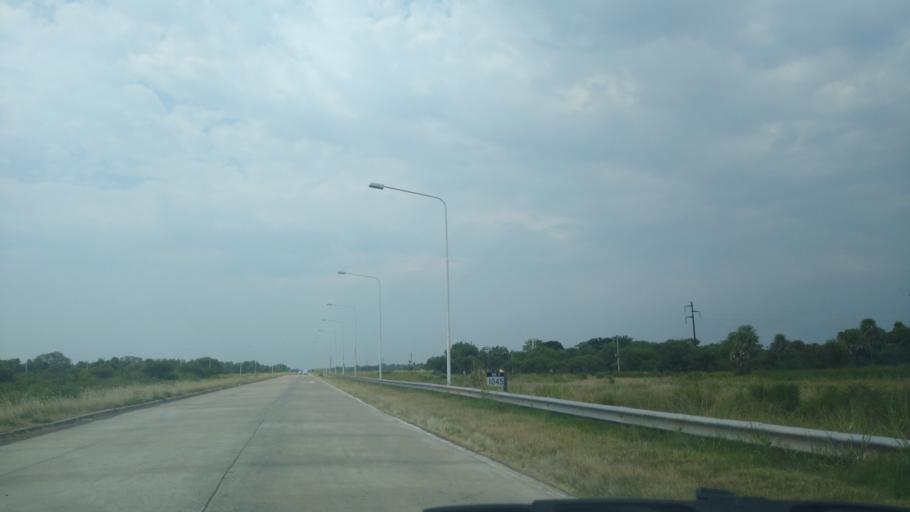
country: AR
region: Chaco
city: Margarita Belen
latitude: -27.0881
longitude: -58.9574
